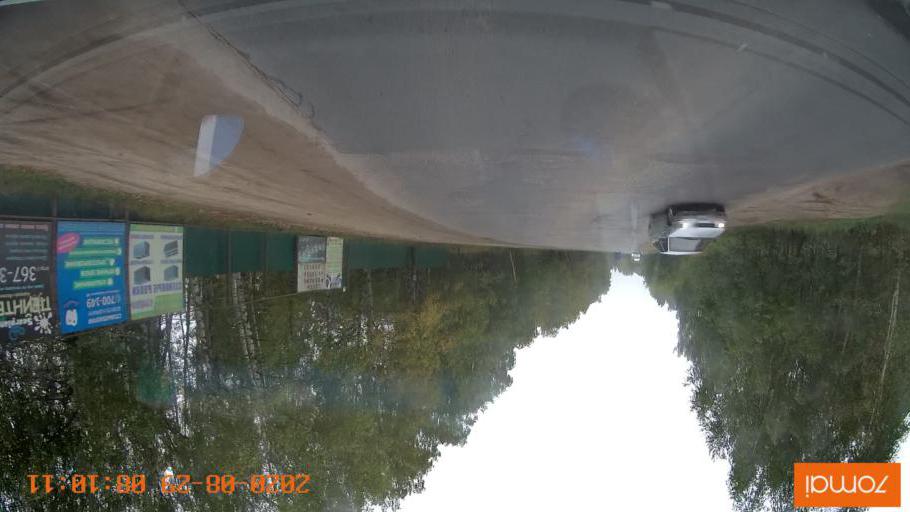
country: RU
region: Ivanovo
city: Kokhma
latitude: 56.9655
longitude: 41.0630
